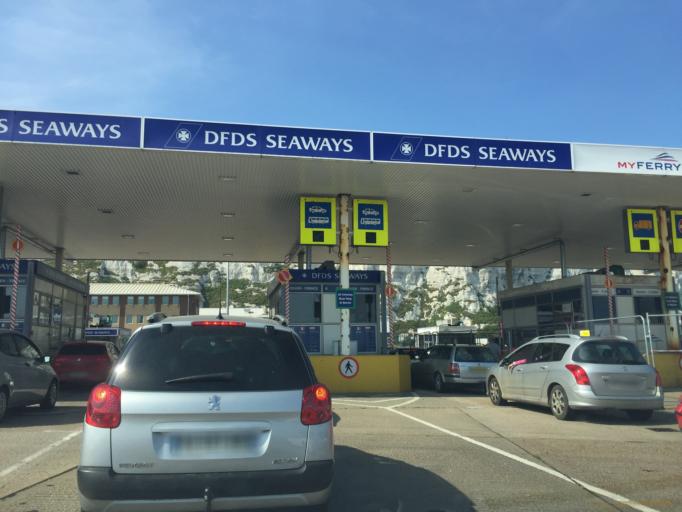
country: GB
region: England
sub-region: Kent
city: Dover
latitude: 51.1290
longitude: 1.3415
